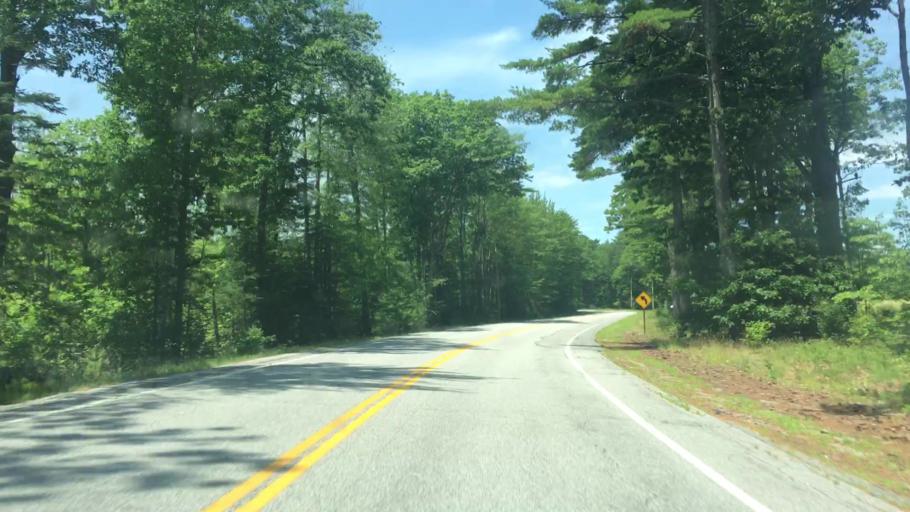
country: US
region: Maine
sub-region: Kennebec County
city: Wayne
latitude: 44.3505
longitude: -70.1026
